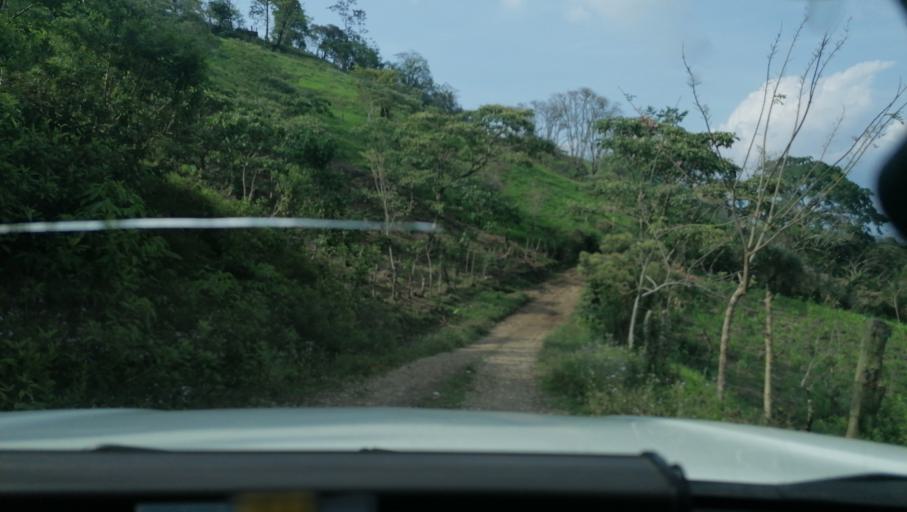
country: MX
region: Chiapas
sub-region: Tapilula
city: San Francisco Jacona
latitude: 17.3042
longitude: -93.1032
